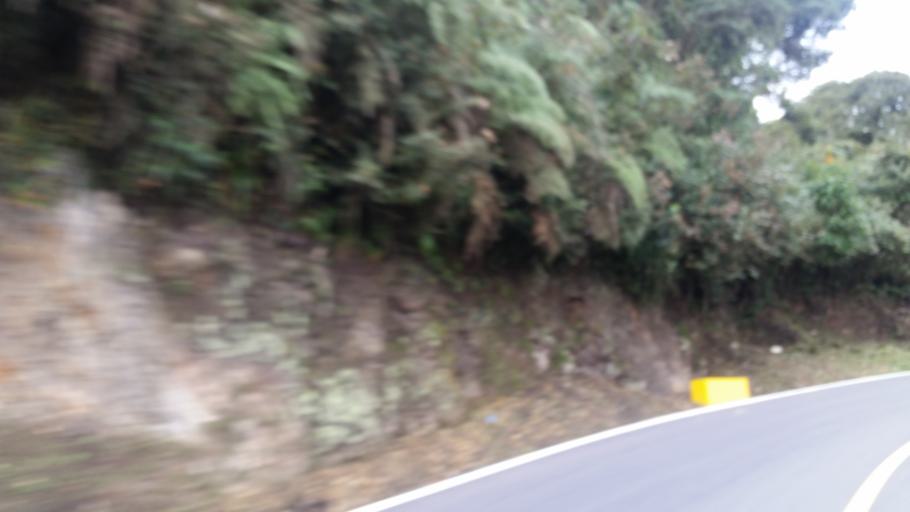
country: CO
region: Cundinamarca
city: Choachi
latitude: 4.5557
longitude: -73.9487
